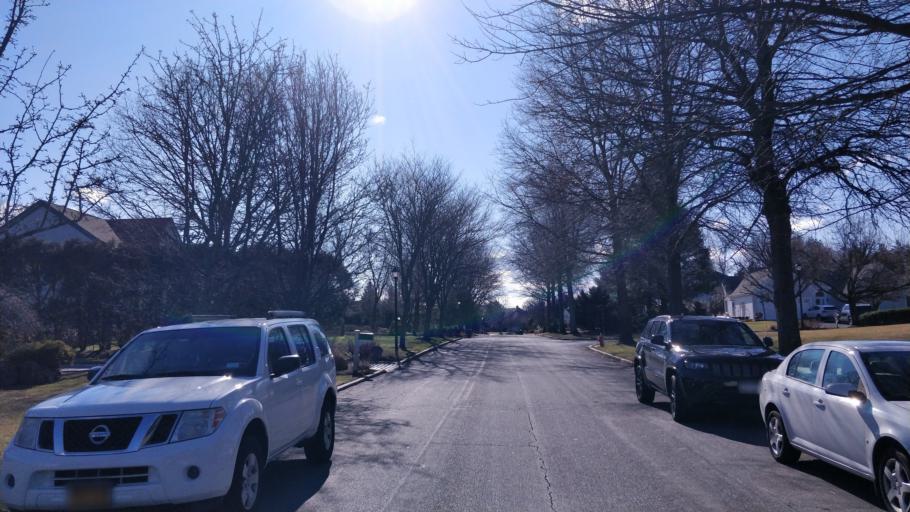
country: US
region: New York
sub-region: Suffolk County
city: Saint James
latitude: 40.8900
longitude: -73.1447
